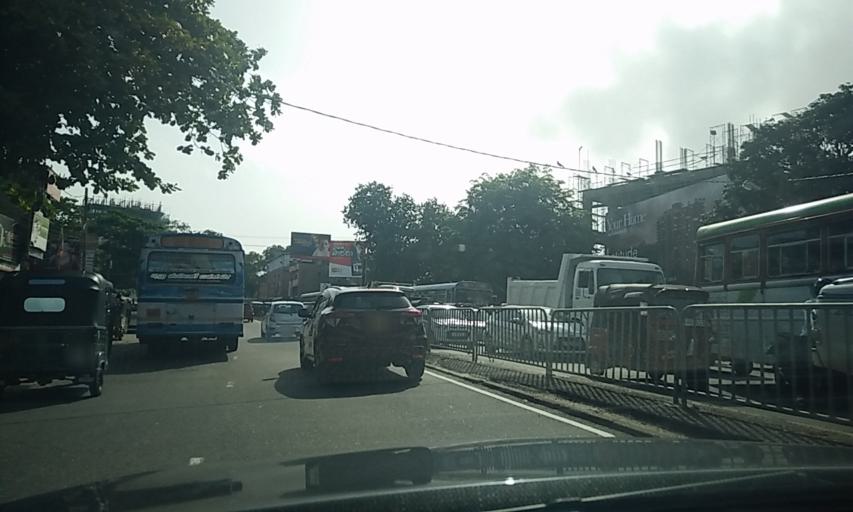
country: LK
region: Western
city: Pita Kotte
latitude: 6.8786
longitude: 79.8737
